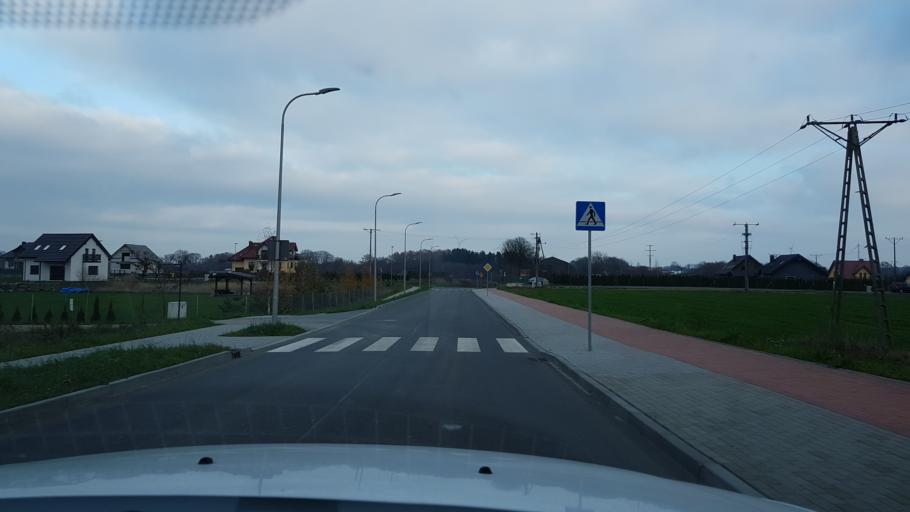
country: PL
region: West Pomeranian Voivodeship
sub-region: Powiat kolobrzeski
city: Goscino
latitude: 54.0548
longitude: 15.6554
